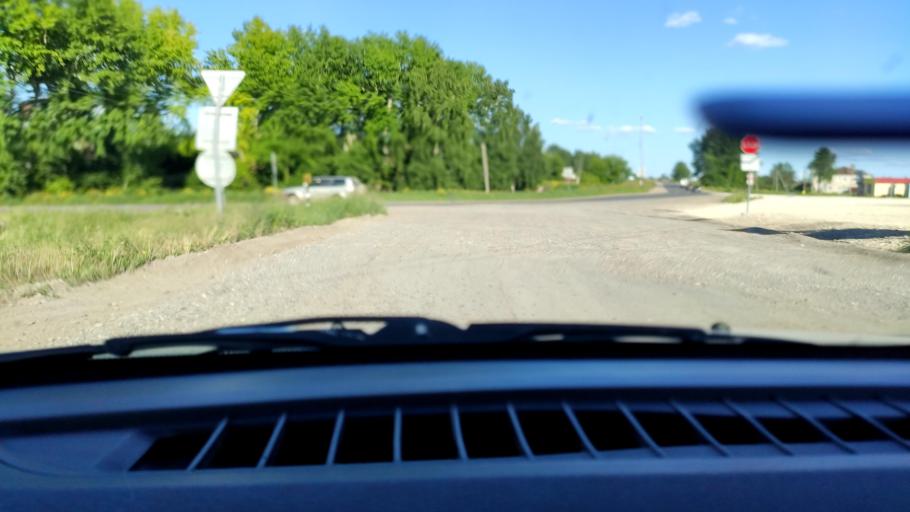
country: RU
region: Perm
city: Orda
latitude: 57.1914
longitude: 56.9041
